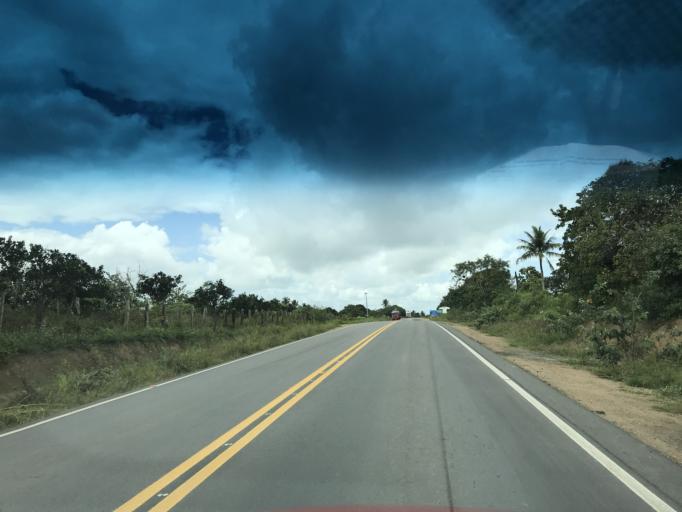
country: BR
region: Bahia
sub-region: Conceicao Do Almeida
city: Conceicao do Almeida
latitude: -12.6922
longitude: -39.2461
